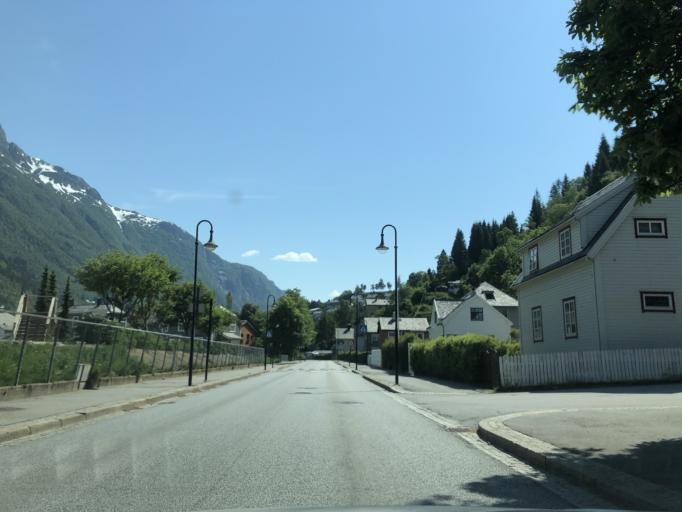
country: NO
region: Hordaland
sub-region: Odda
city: Odda
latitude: 60.0688
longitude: 6.5415
